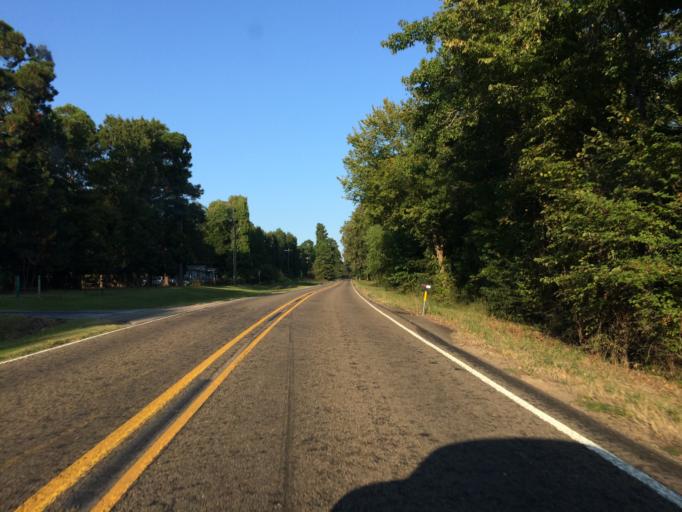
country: US
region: Texas
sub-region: Wood County
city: Mineola
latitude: 32.6747
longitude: -95.4480
